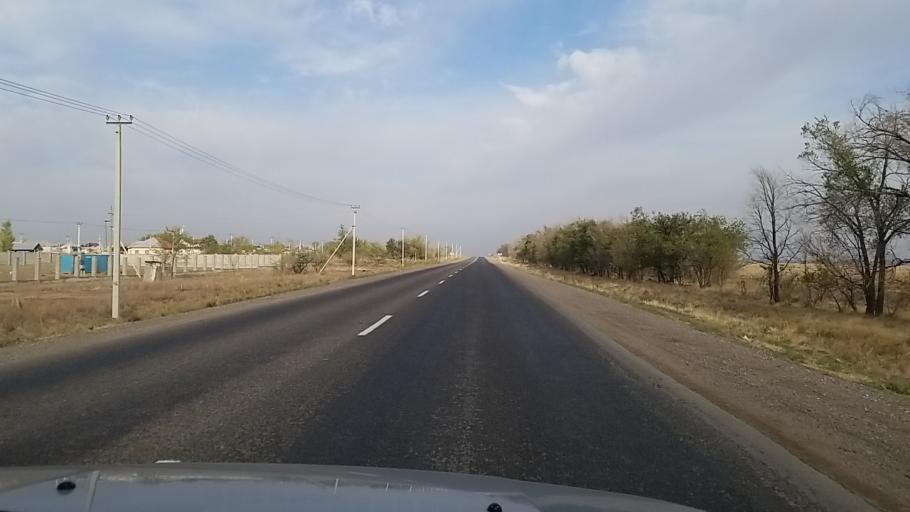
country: KZ
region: Almaty Oblysy
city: Burunday
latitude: 43.4824
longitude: 76.6756
